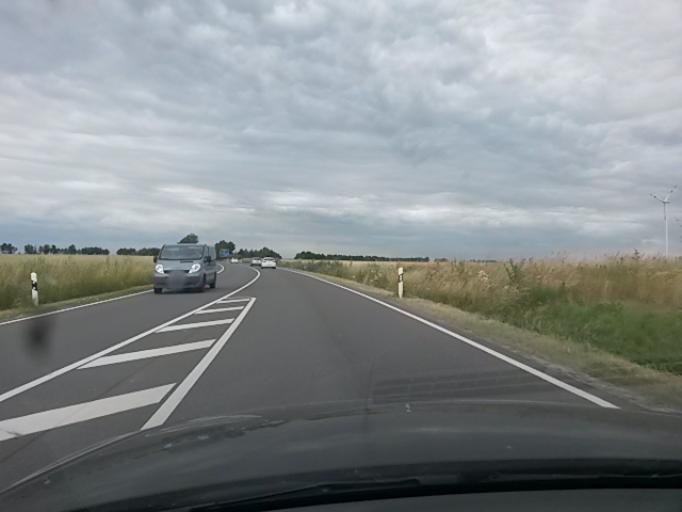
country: DE
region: Bavaria
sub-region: Regierungsbezirk Unterfranken
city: Buchbrunn
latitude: 49.7584
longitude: 10.1155
